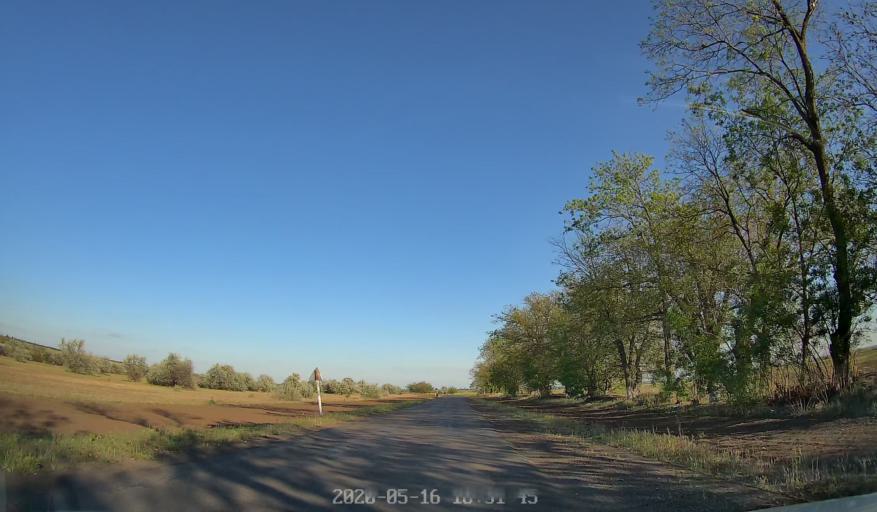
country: UA
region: Odessa
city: Lymanske
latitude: 46.5419
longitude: 30.0460
